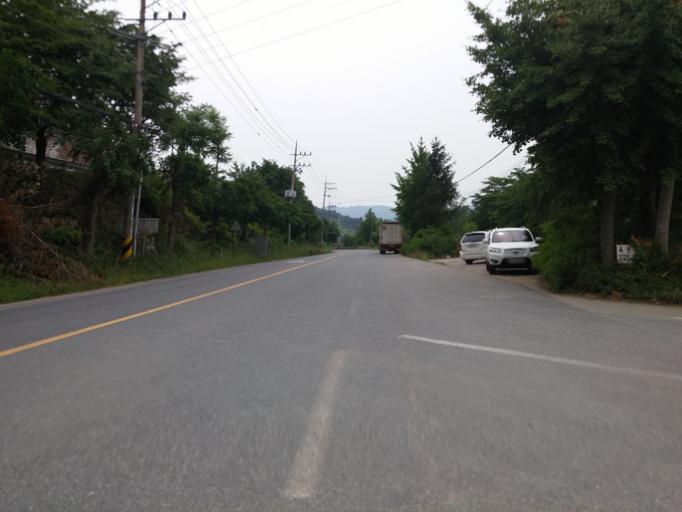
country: KR
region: Chungcheongbuk-do
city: Okcheon
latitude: 36.3012
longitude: 127.5450
